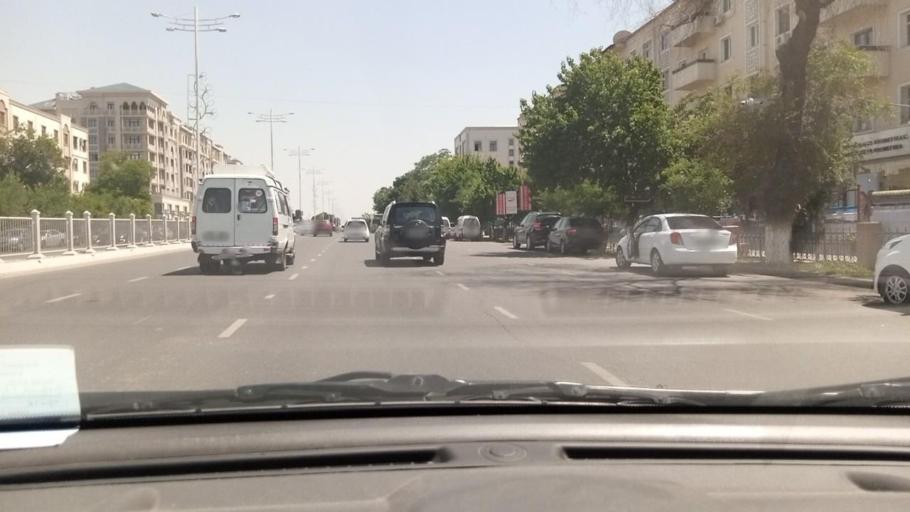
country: UZ
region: Toshkent Shahri
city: Tashkent
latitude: 41.2912
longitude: 69.2243
